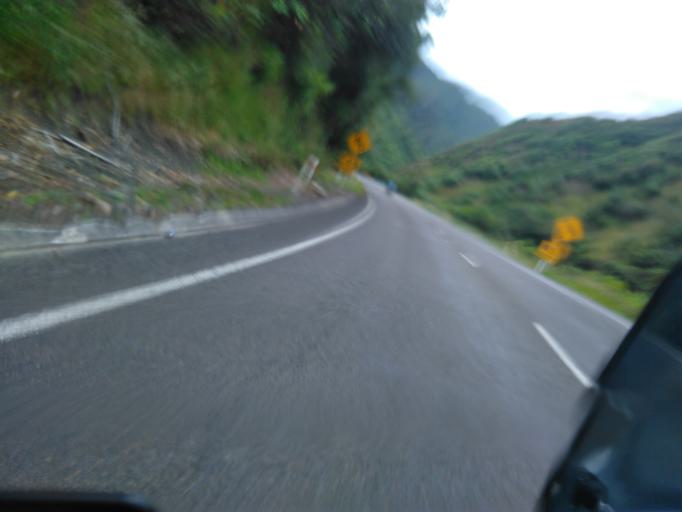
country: NZ
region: Bay of Plenty
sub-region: Opotiki District
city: Opotiki
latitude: -38.3373
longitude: 177.4213
